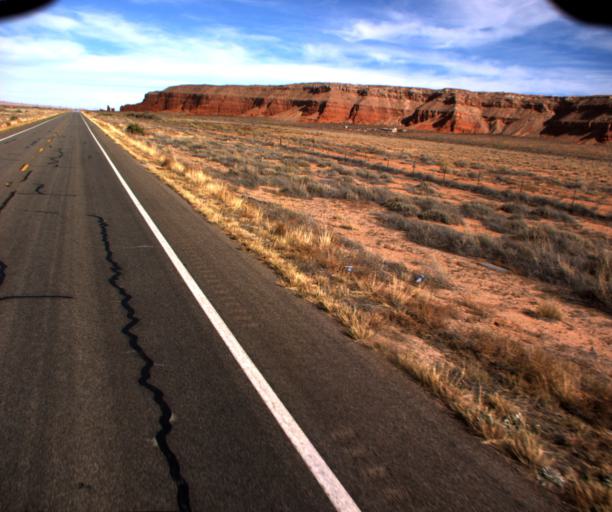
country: US
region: Arizona
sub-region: Navajo County
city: Kayenta
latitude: 36.7654
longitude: -110.0351
